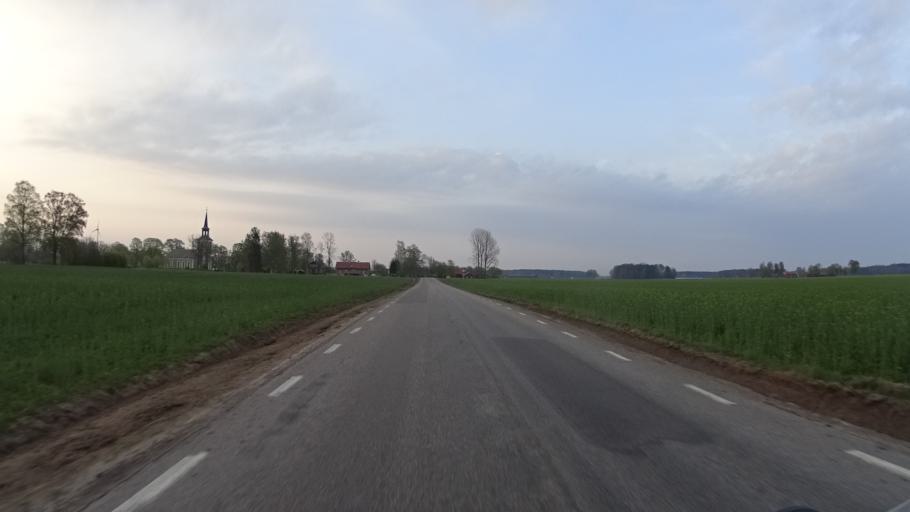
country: SE
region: Vaestra Goetaland
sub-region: Gotene Kommun
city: Kallby
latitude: 58.4753
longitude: 13.3240
